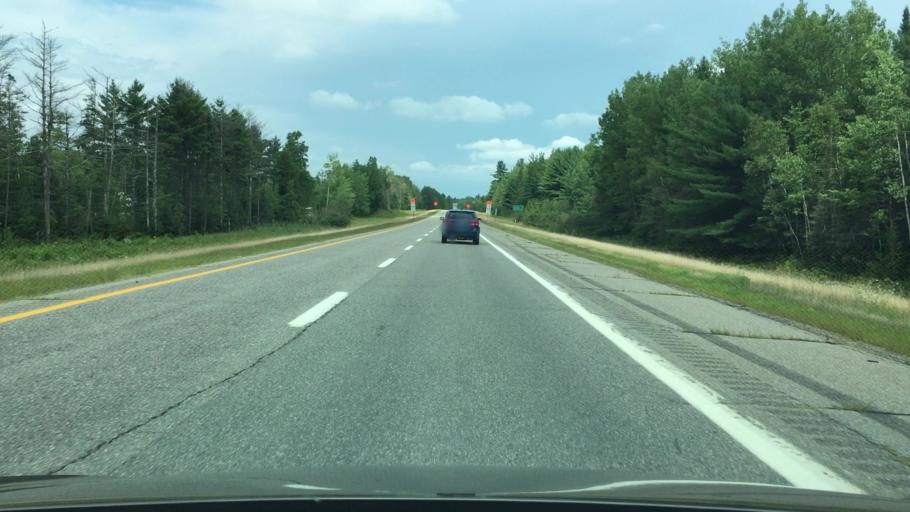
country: US
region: Maine
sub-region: Penobscot County
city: Howland
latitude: 45.2547
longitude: -68.6793
